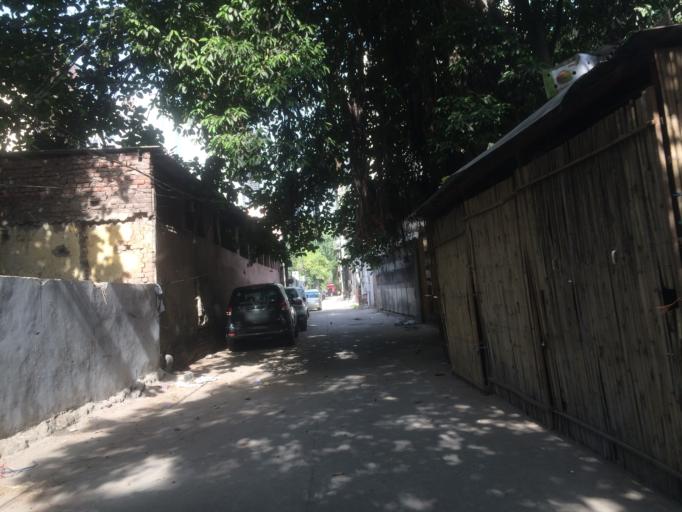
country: IN
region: NCT
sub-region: New Delhi
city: New Delhi
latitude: 28.5661
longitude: 77.2478
